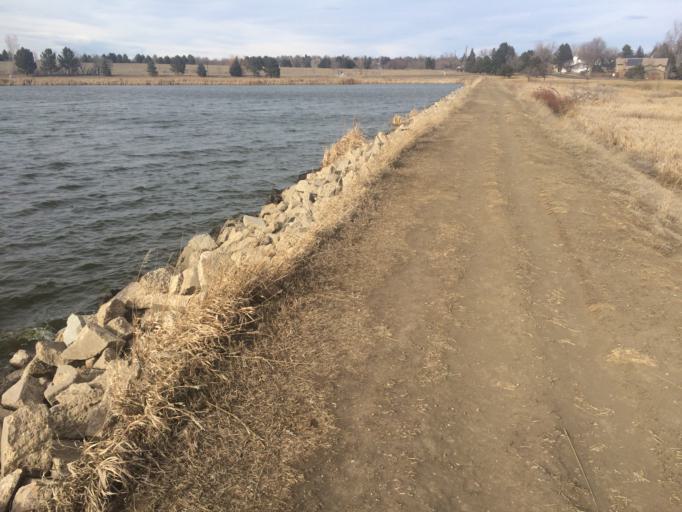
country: US
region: Colorado
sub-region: Broomfield County
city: Broomfield
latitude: 39.9203
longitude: -105.0628
